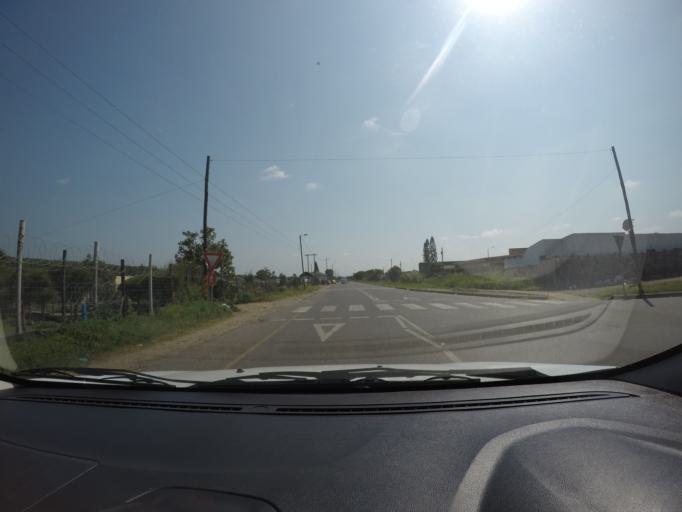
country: ZA
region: KwaZulu-Natal
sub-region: uThungulu District Municipality
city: eSikhawini
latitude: -28.8816
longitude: 31.8893
